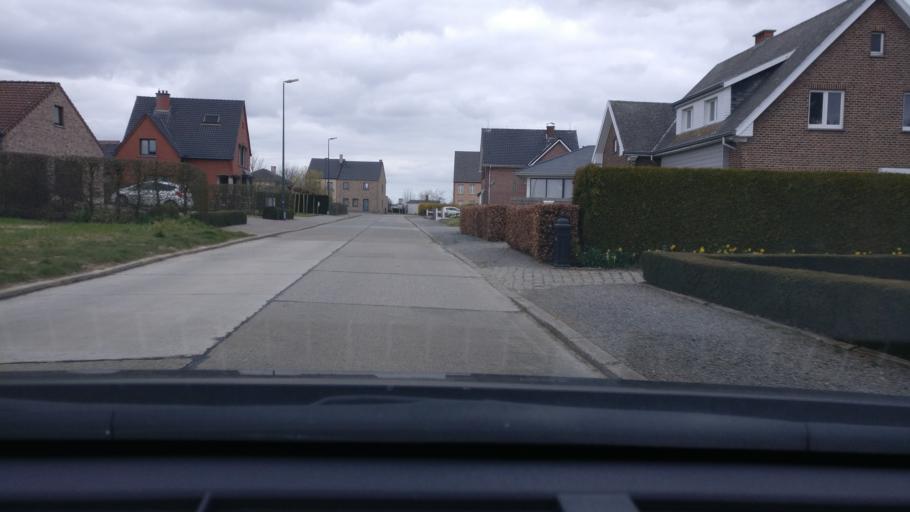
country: BE
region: Flanders
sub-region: Provincie Vlaams-Brabant
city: Overijse
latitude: 50.8064
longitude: 4.5467
